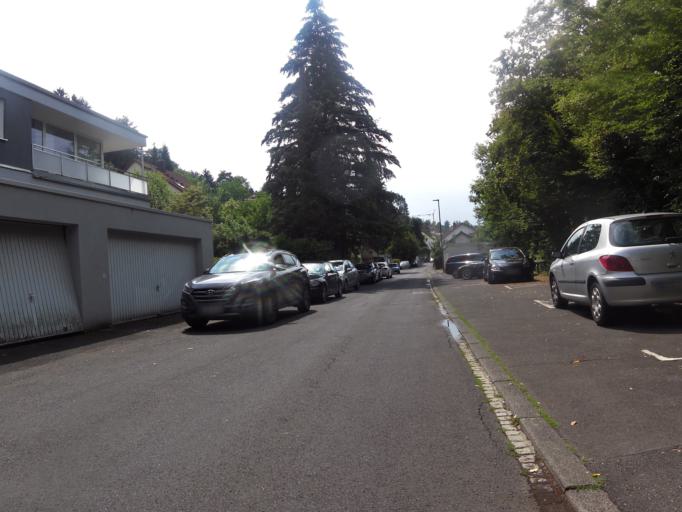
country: DE
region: Bavaria
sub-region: Regierungsbezirk Unterfranken
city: Hochberg
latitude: 49.7855
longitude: 9.8953
